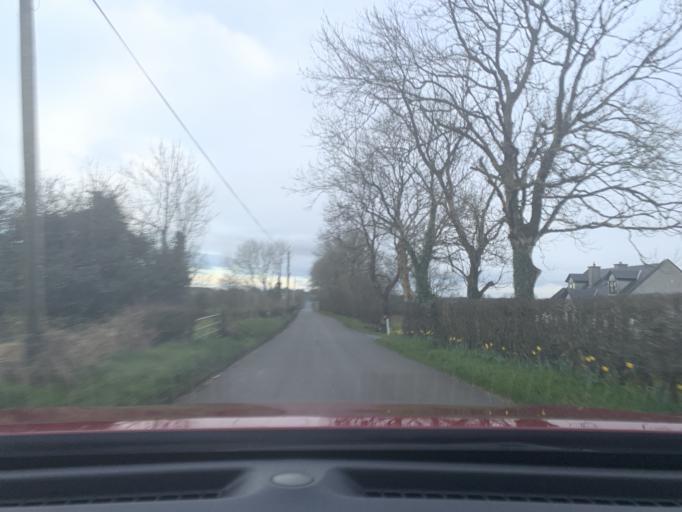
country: IE
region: Connaught
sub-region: Roscommon
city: Ballaghaderreen
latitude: 53.8756
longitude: -8.5602
